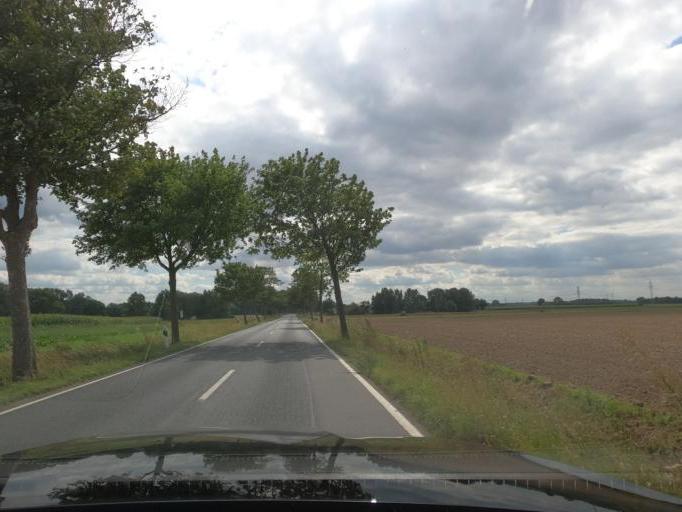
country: DE
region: Lower Saxony
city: Lehrte
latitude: 52.3489
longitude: 10.0284
